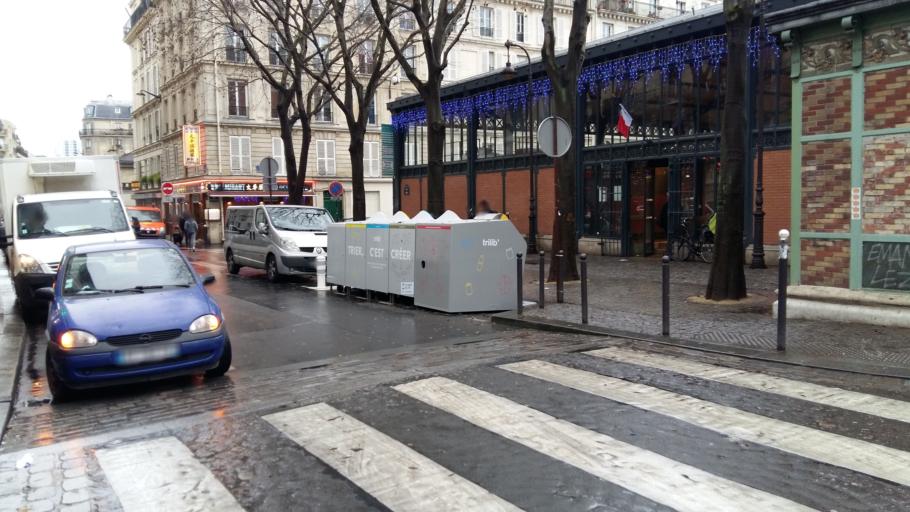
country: FR
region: Ile-de-France
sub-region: Paris
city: Saint-Ouen
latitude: 48.8913
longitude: 2.3613
